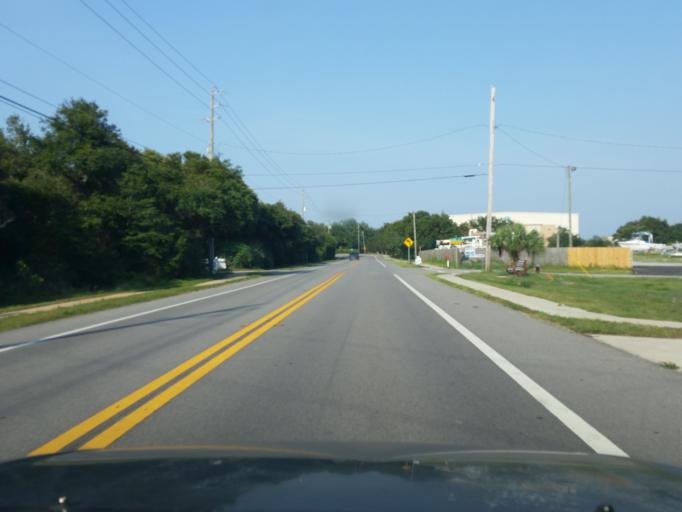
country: US
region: Florida
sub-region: Escambia County
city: Warrington
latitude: 30.3291
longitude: -87.3596
